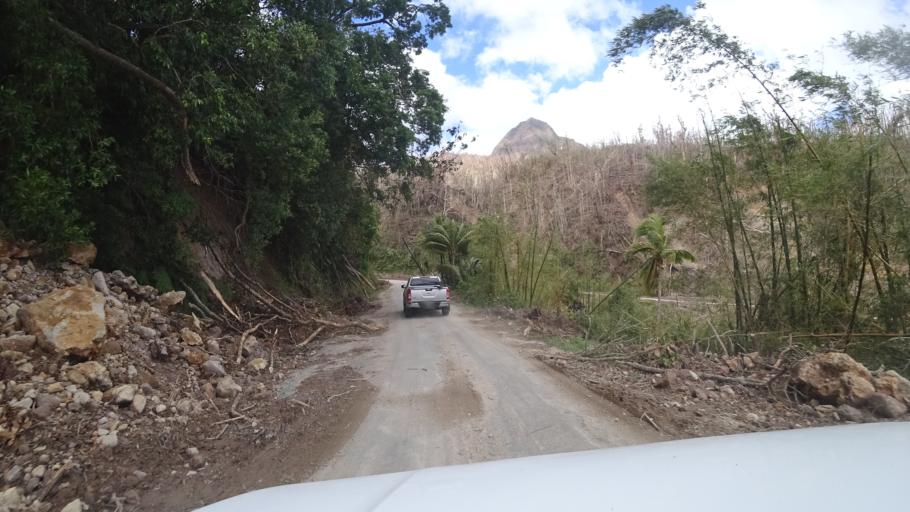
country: DM
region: Saint Luke
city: Pointe Michel
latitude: 15.2669
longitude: -61.3412
